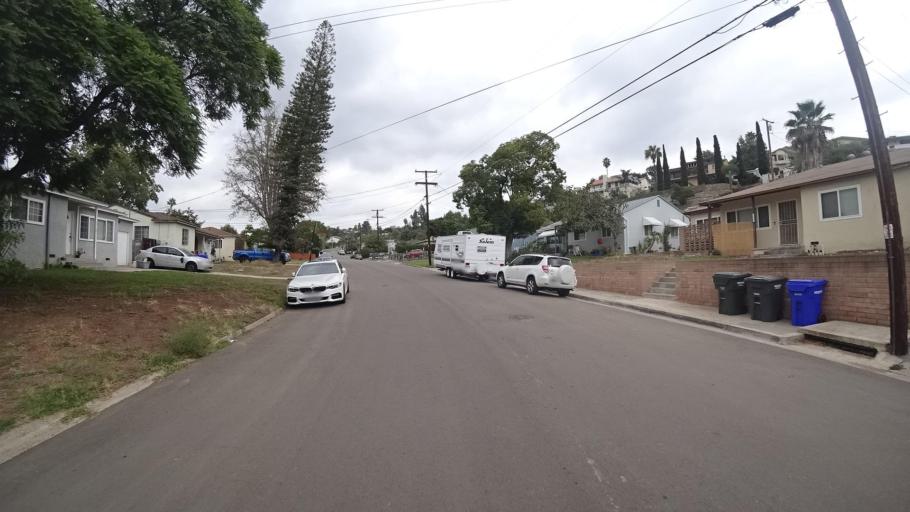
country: US
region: California
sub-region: San Diego County
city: Spring Valley
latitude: 32.7449
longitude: -117.0138
